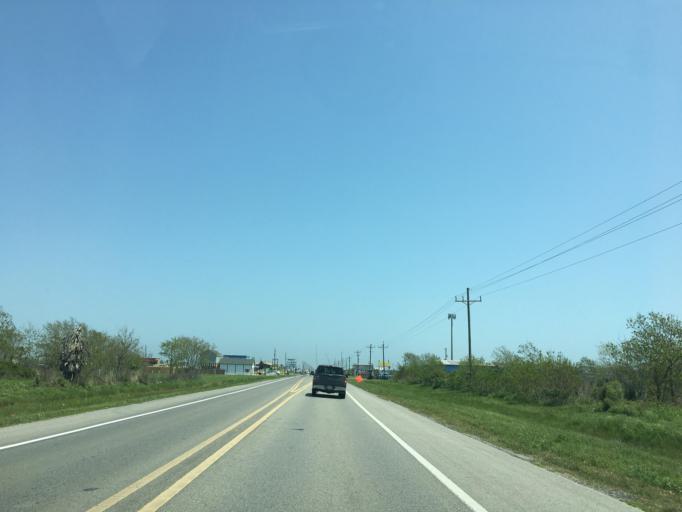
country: US
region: Texas
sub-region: Galveston County
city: Bolivar Peninsula
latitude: 29.4400
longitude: -94.6700
